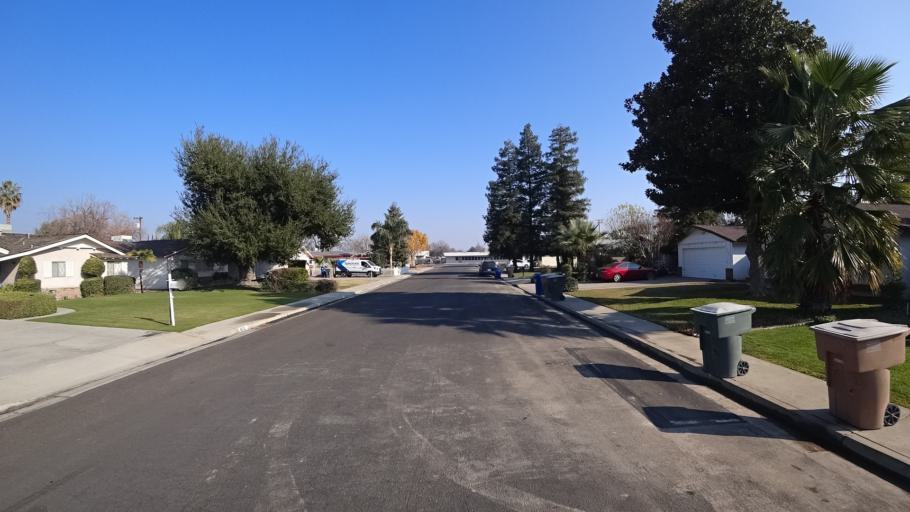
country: US
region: California
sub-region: Kern County
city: Bakersfield
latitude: 35.3436
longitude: -119.0477
